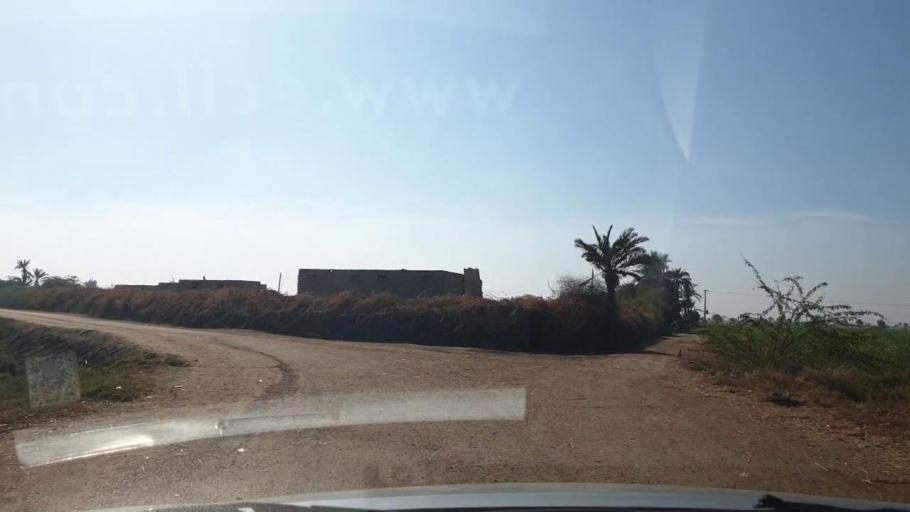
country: PK
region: Sindh
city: Jhol
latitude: 25.8146
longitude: 68.9700
